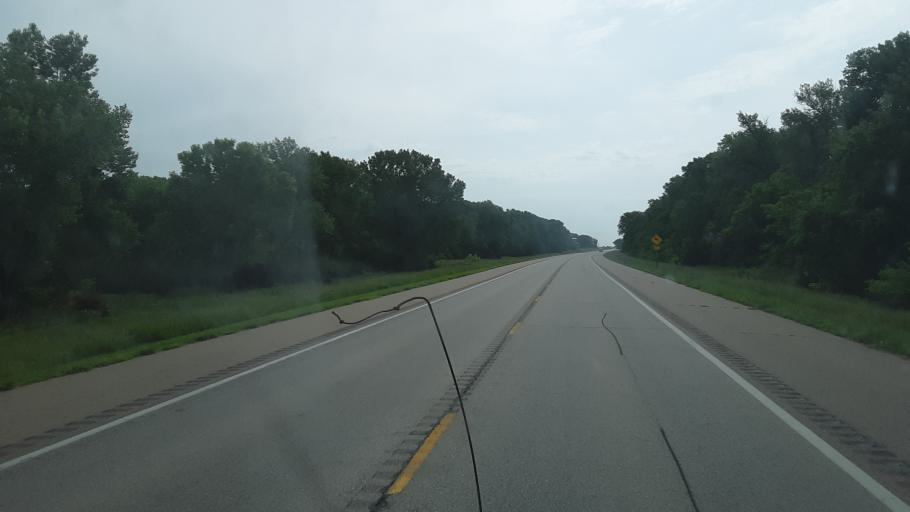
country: US
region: Kansas
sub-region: Stafford County
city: Stafford
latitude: 37.9846
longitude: -98.3725
